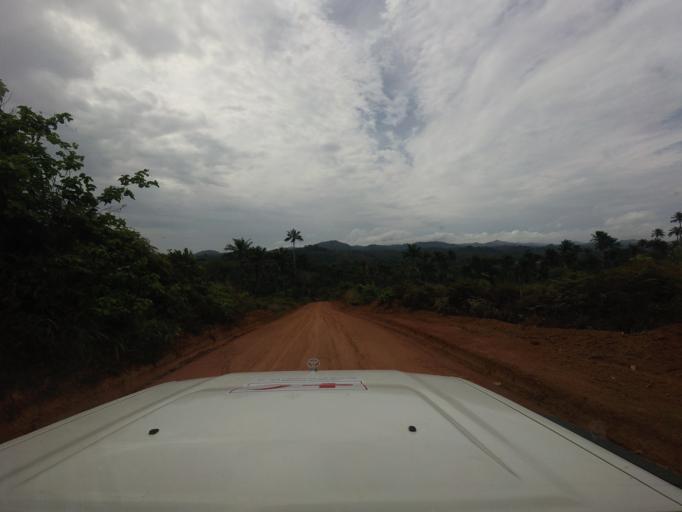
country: SL
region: Eastern Province
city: Buedu
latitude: 8.2221
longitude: -10.2226
